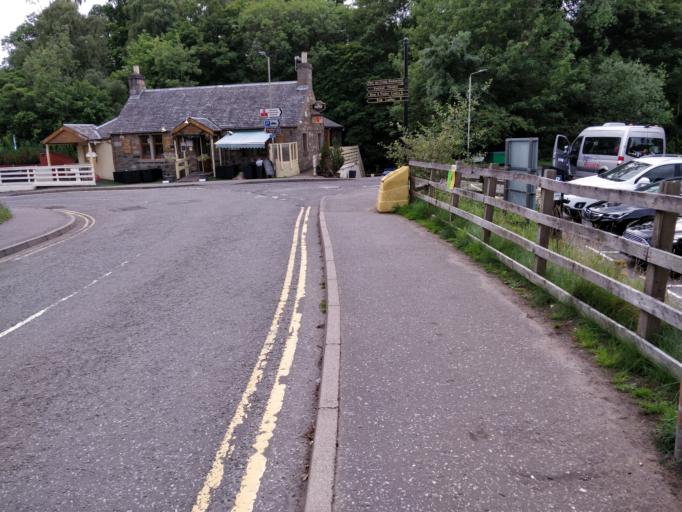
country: GB
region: Scotland
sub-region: Perth and Kinross
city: Pitlochry
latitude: 56.7017
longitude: -3.7326
